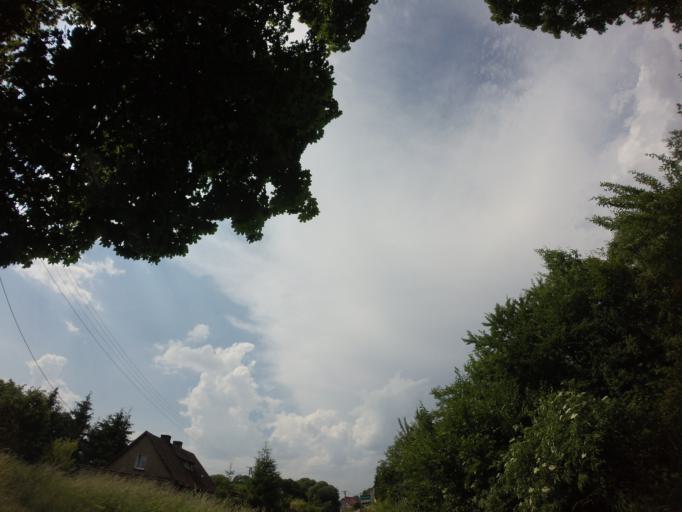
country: PL
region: West Pomeranian Voivodeship
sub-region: Powiat choszczenski
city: Krzecin
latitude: 53.1429
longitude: 15.5527
